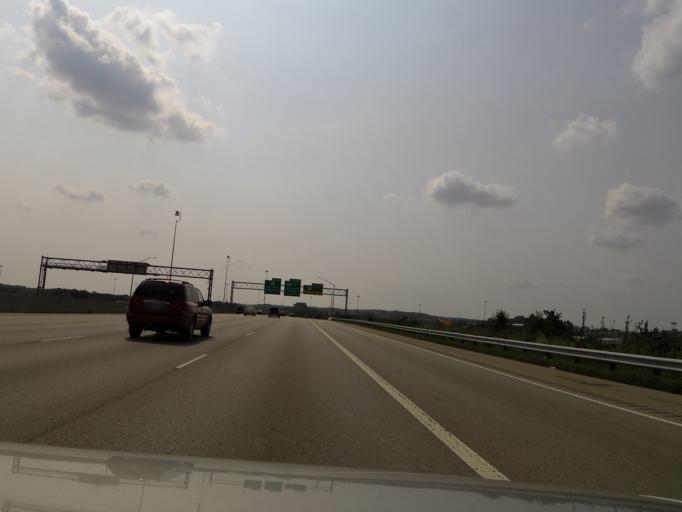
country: US
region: Ohio
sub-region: Hamilton County
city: Glendale
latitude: 39.2944
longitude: -84.4612
